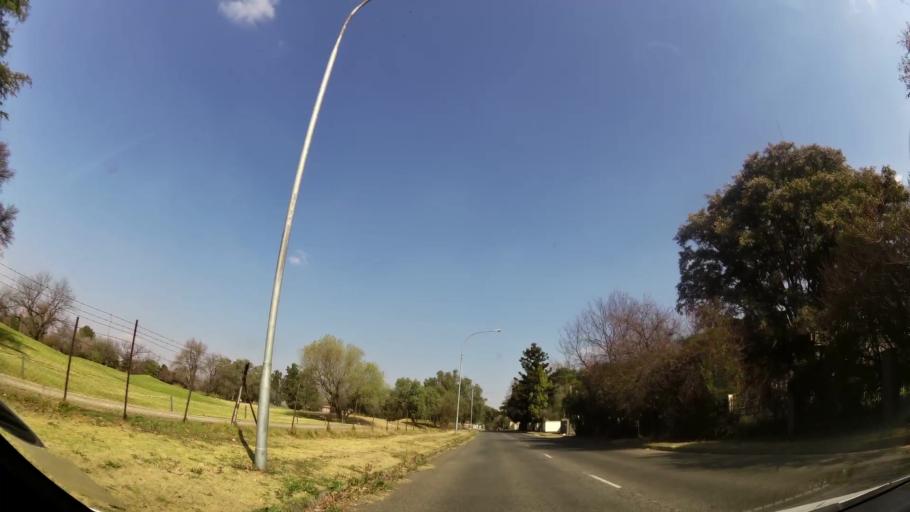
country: ZA
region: Gauteng
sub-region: Ekurhuleni Metropolitan Municipality
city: Benoni
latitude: -26.1845
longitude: 28.2919
